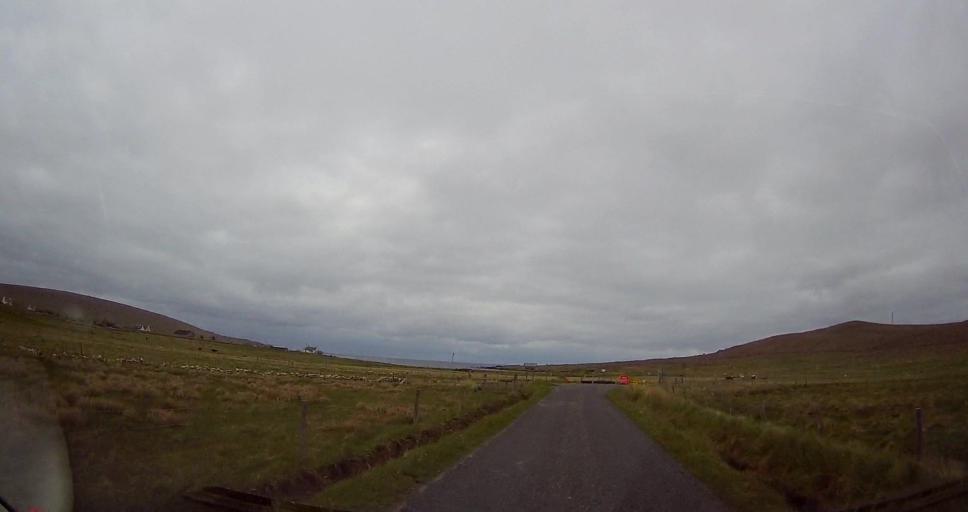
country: GB
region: Scotland
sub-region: Shetland Islands
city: Shetland
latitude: 60.7893
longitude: -0.8424
